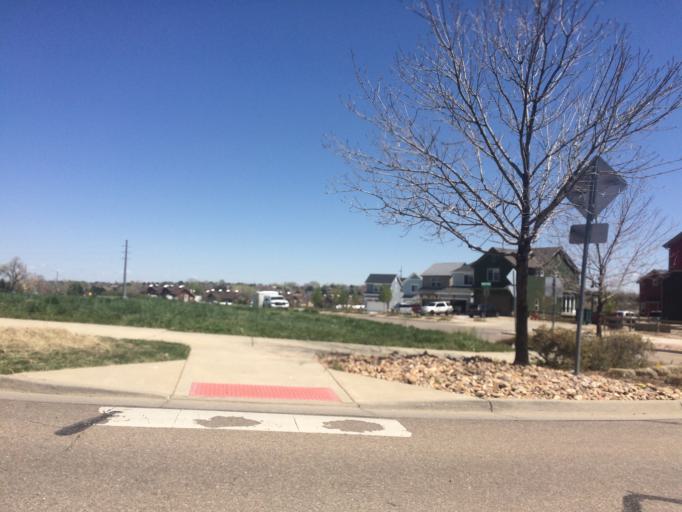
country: US
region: Colorado
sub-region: Boulder County
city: Louisville
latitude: 39.9990
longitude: -105.1340
